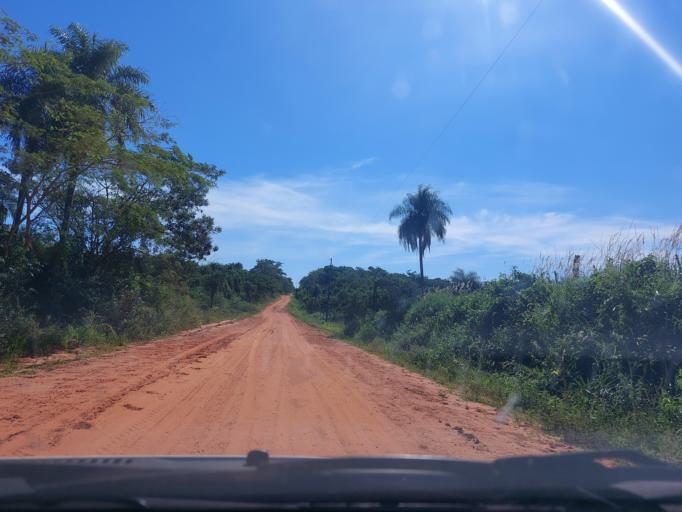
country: PY
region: San Pedro
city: Itacurubi del Rosario
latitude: -24.5475
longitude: -56.5858
